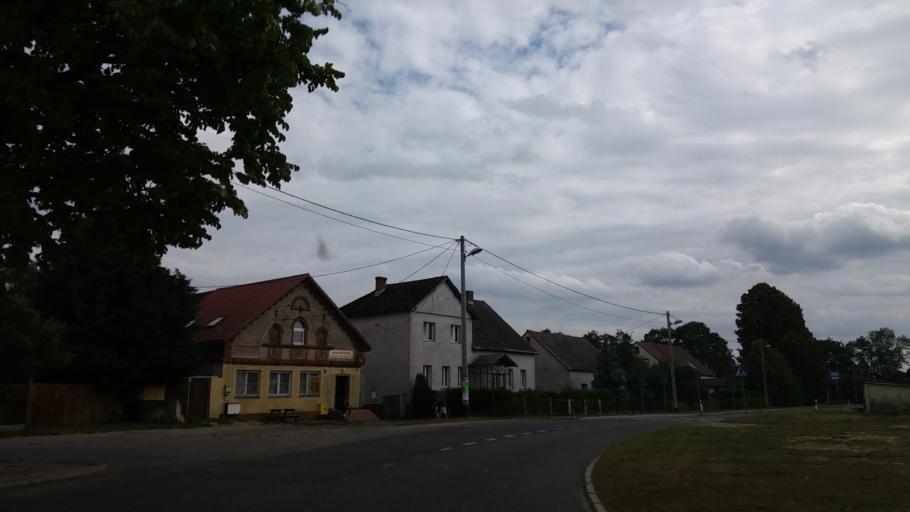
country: PL
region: West Pomeranian Voivodeship
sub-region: Powiat stargardzki
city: Kobylanka
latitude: 53.3239
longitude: 14.8559
